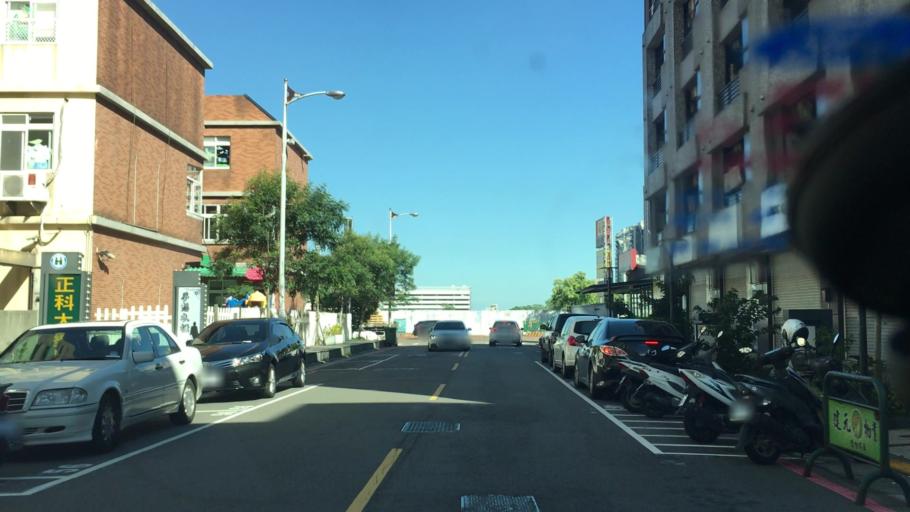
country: TW
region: Taiwan
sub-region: Hsinchu
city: Zhubei
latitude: 24.8223
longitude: 121.0078
